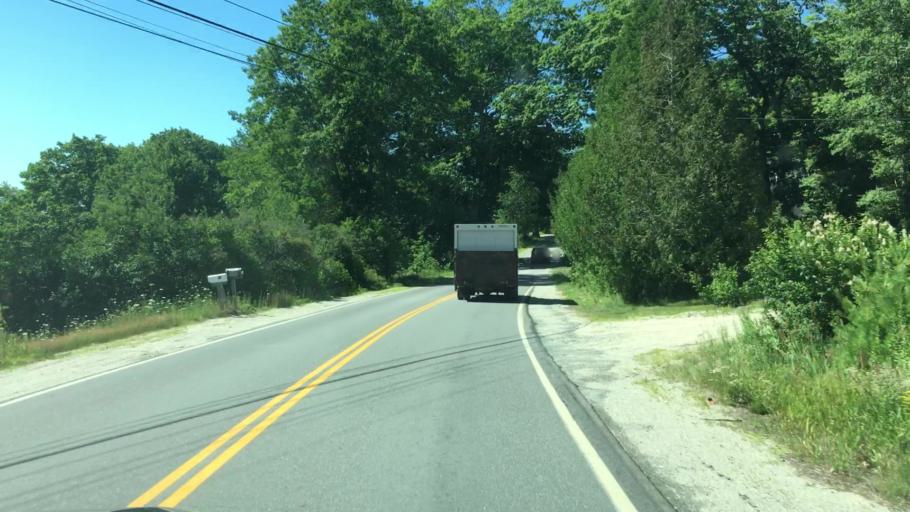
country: US
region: Maine
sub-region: Hancock County
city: Sedgwick
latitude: 44.3482
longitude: -68.5875
